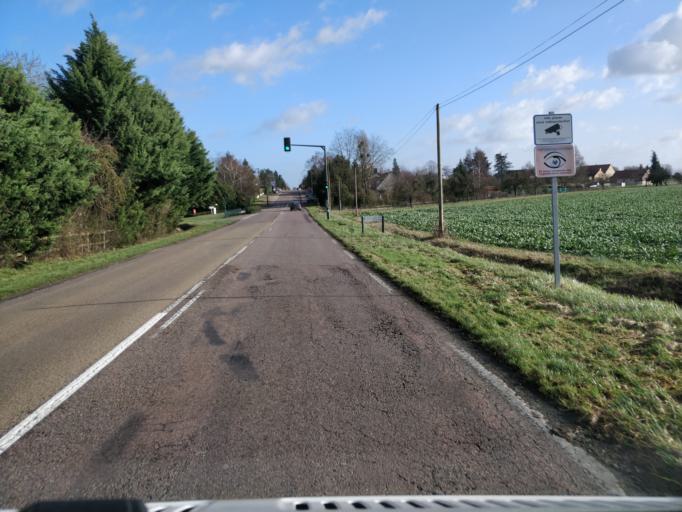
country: FR
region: Bourgogne
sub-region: Departement de l'Yonne
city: Cheroy
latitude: 48.2013
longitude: 2.9861
